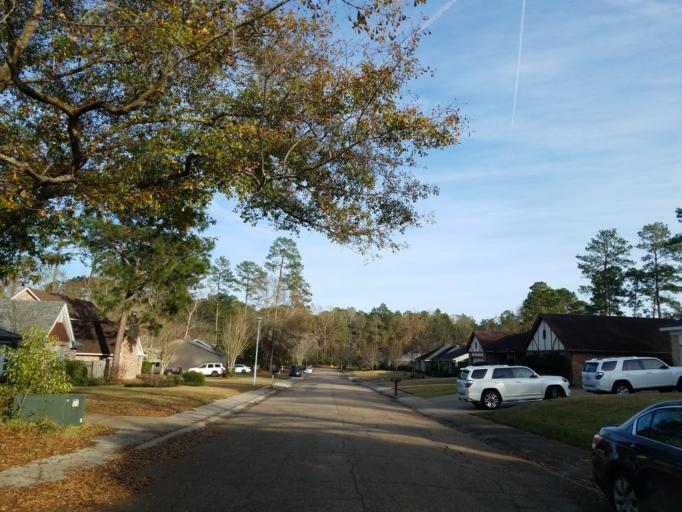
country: US
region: Mississippi
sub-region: Lamar County
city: West Hattiesburg
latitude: 31.3144
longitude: -89.3501
